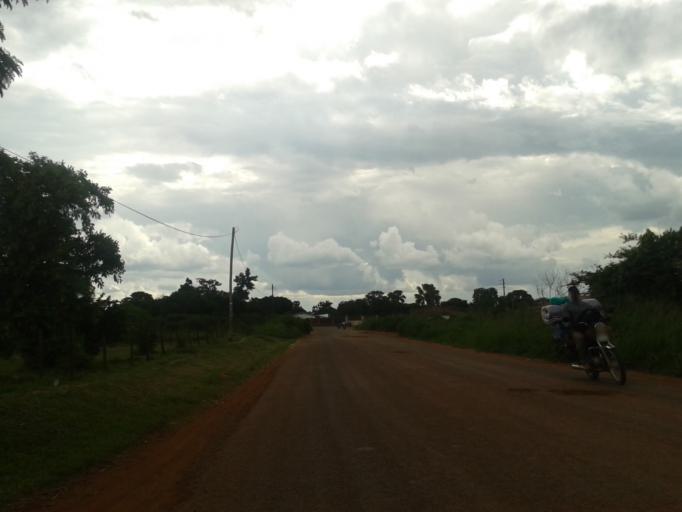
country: UG
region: Northern Region
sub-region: Gulu District
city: Gulu
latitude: 2.7846
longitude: 32.3089
